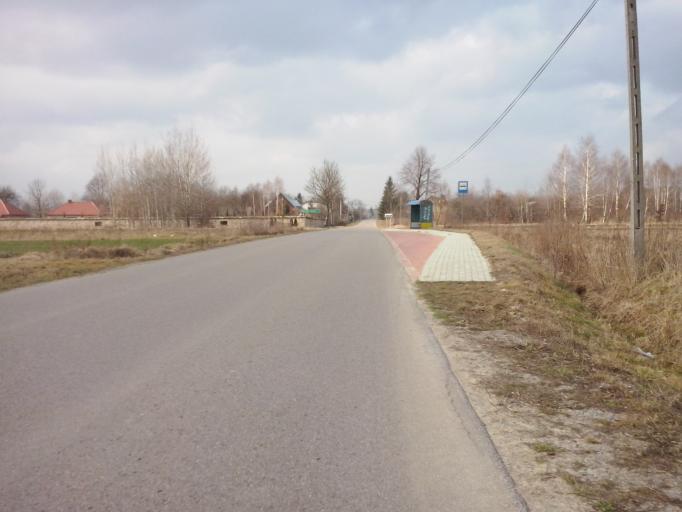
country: PL
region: Subcarpathian Voivodeship
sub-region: Powiat nizanski
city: Krzeszow
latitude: 50.4209
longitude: 22.3260
